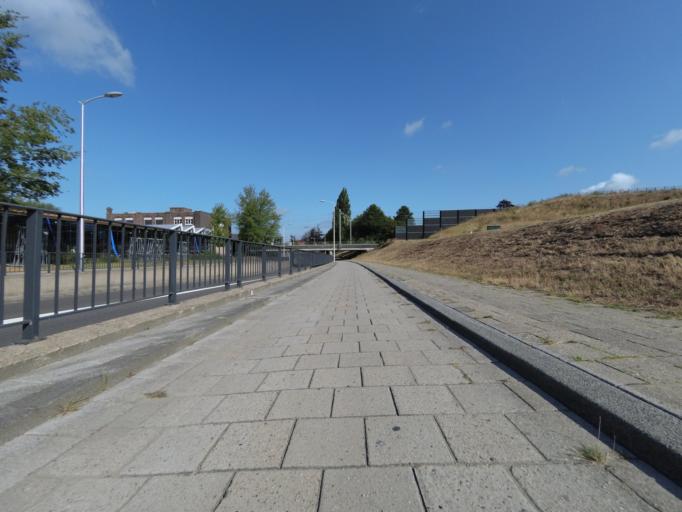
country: NL
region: Overijssel
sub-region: Gemeente Oldenzaal
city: Oldenzaal
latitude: 52.3053
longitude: 6.9311
